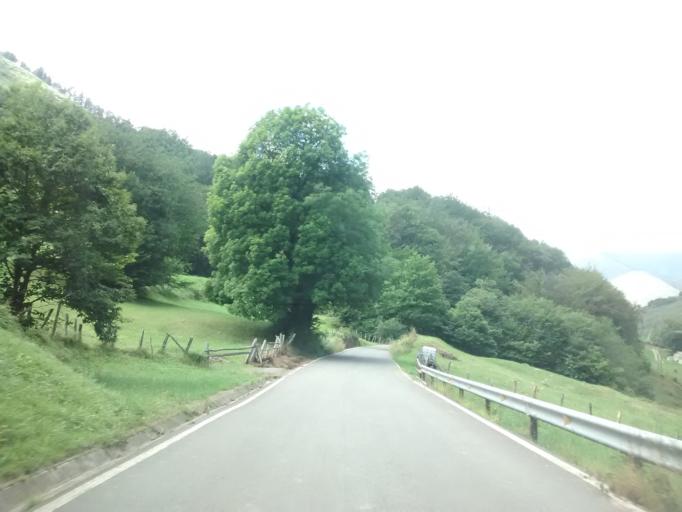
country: ES
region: Cantabria
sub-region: Provincia de Cantabria
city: Ruente
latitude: 43.1919
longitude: -4.2723
